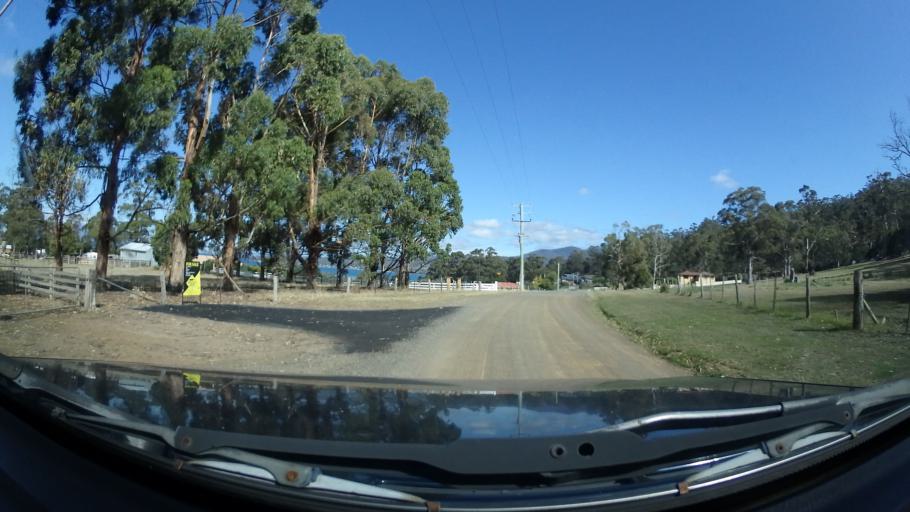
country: AU
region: Tasmania
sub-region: Sorell
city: Sorell
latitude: -42.5443
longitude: 147.8750
